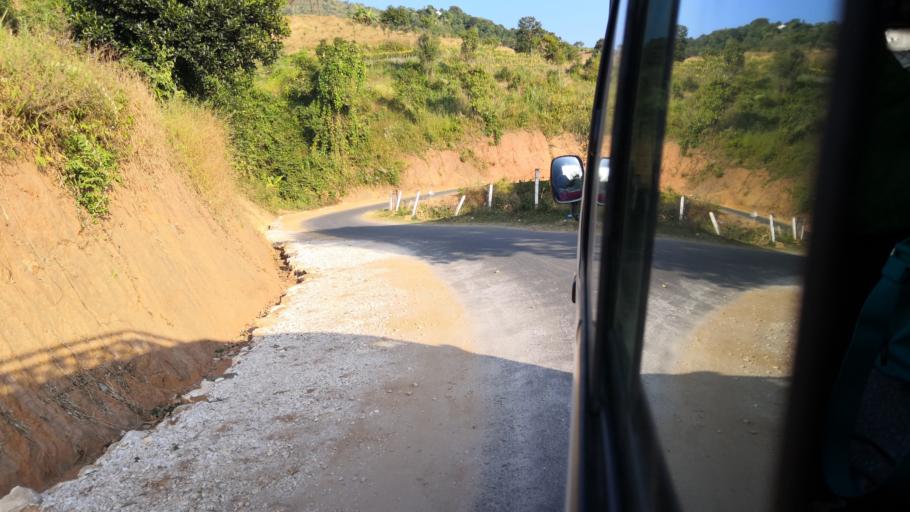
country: MM
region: Mandalay
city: Mogok
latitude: 22.9046
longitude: 96.3870
